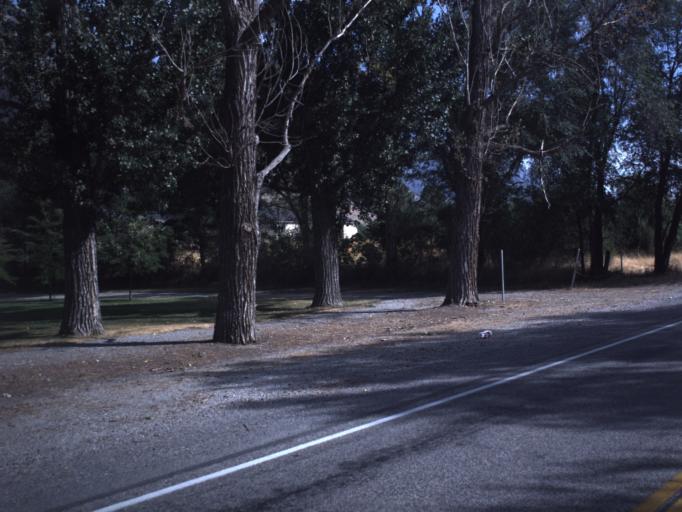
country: US
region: Utah
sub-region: Box Elder County
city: Elwood
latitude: 41.7068
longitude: -112.0902
